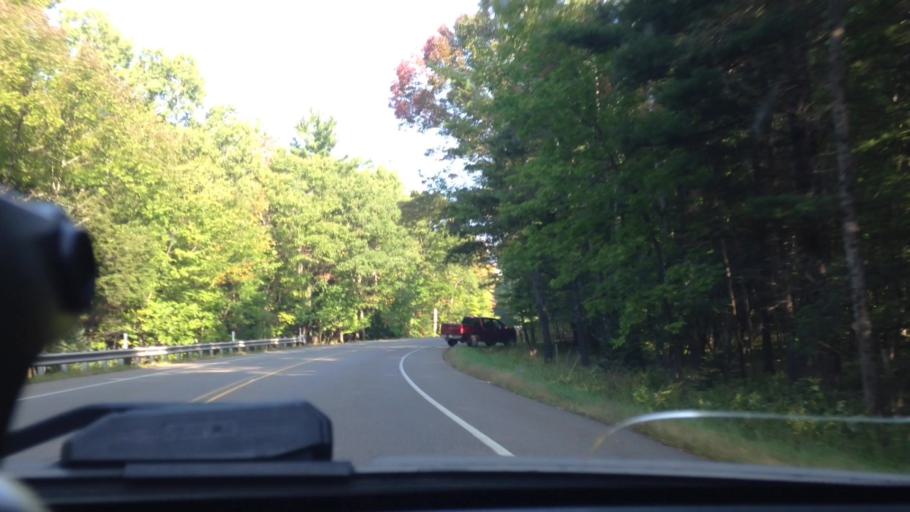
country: US
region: Michigan
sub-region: Dickinson County
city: Quinnesec
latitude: 45.8191
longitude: -87.9881
